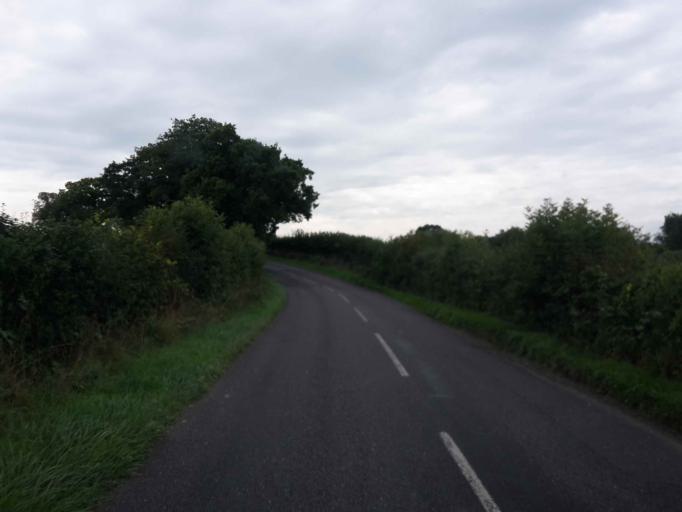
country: GB
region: England
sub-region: West Sussex
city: Rudgwick
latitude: 51.0726
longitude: -0.4517
